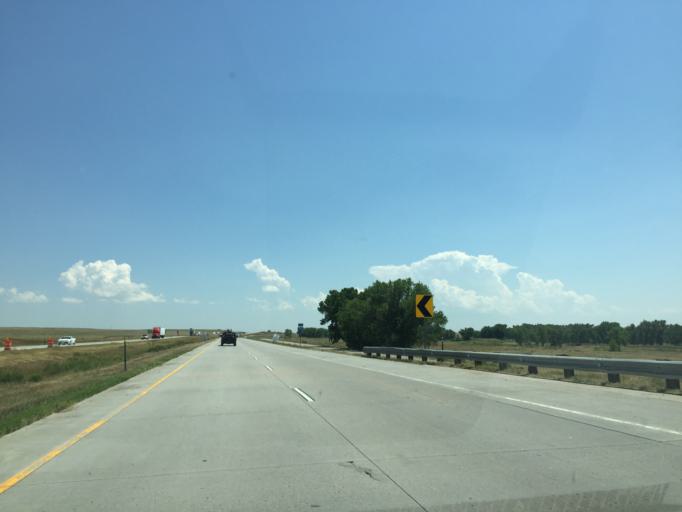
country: US
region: Colorado
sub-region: Arapahoe County
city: Byers
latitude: 39.4980
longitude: -103.9664
